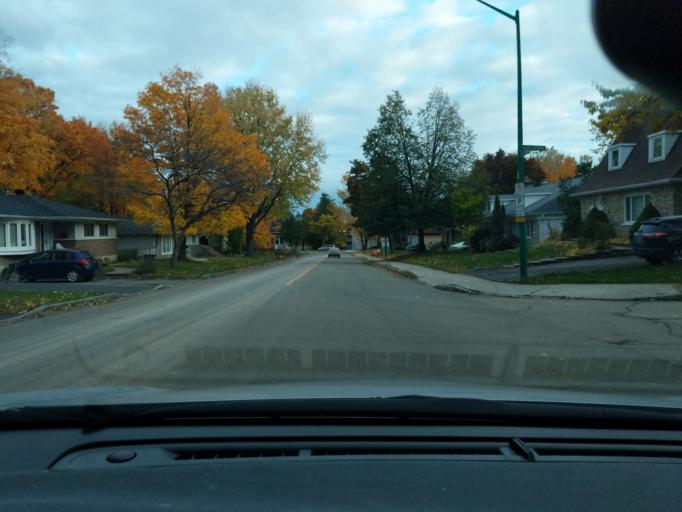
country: CA
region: Quebec
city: L'Ancienne-Lorette
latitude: 46.7602
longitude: -71.2885
